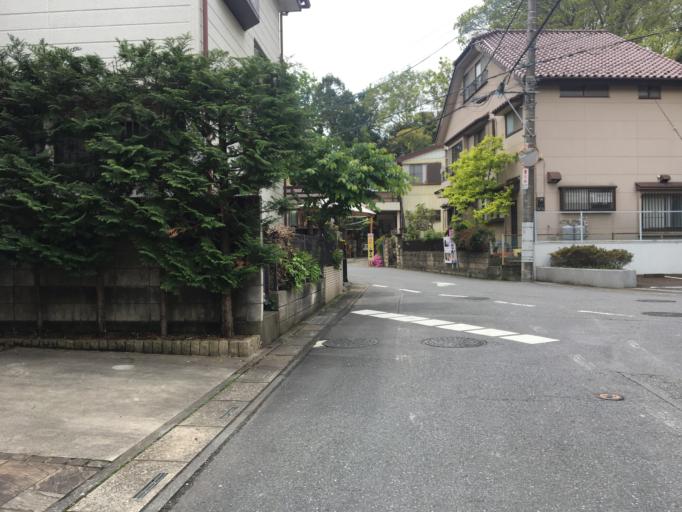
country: JP
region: Saitama
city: Oi
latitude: 35.8496
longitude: 139.5436
